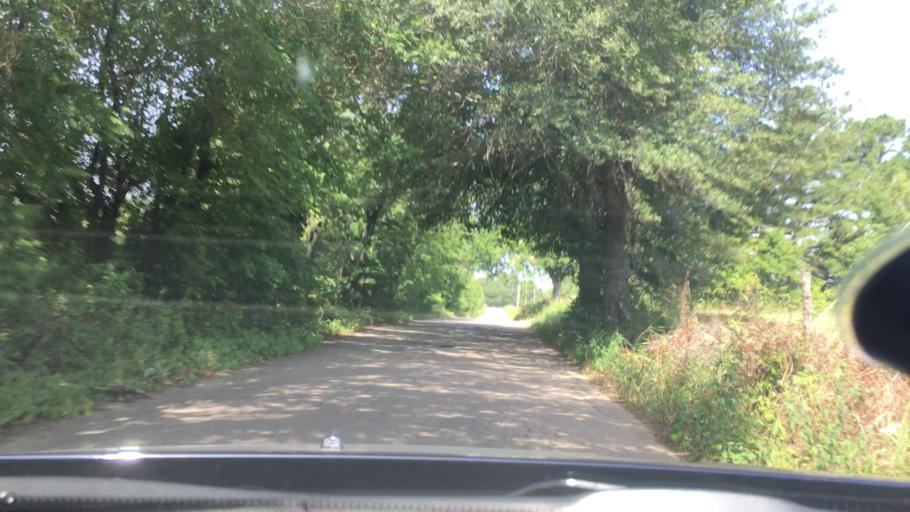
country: US
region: Oklahoma
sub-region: Atoka County
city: Atoka
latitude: 34.3603
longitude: -96.1663
